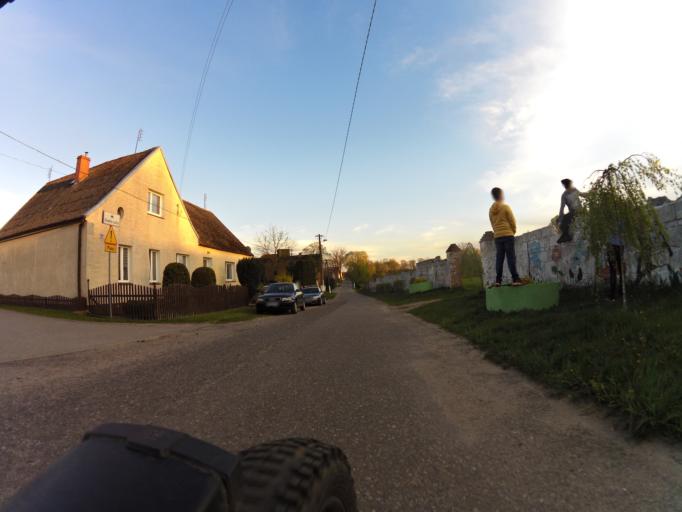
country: PL
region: West Pomeranian Voivodeship
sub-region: Powiat lobeski
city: Lobez
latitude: 53.6991
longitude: 15.6456
